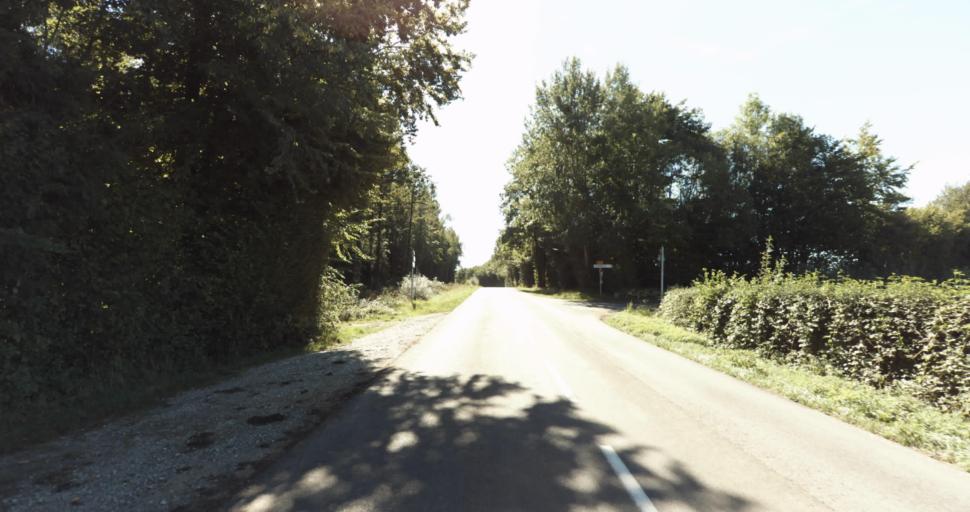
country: FR
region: Lower Normandy
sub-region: Departement de l'Orne
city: Gace
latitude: 48.7899
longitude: 0.2209
